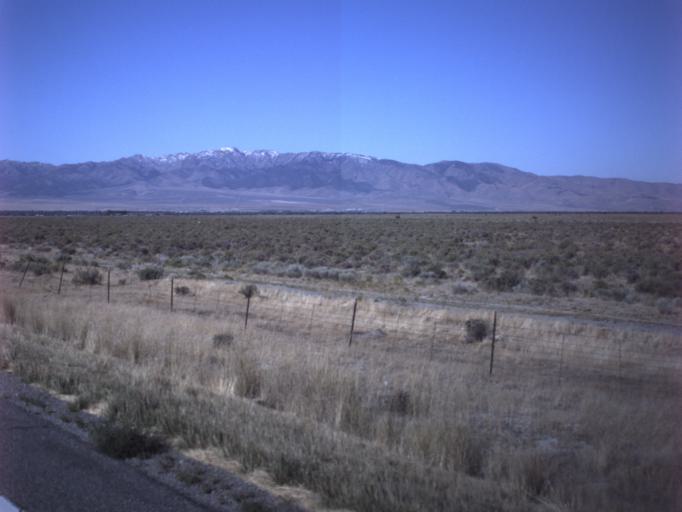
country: US
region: Utah
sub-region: Tooele County
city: Erda
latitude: 40.6121
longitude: -112.3756
